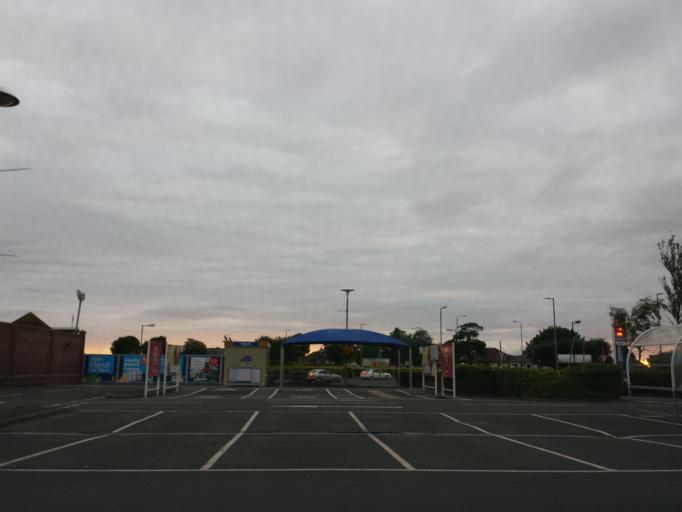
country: GB
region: Scotland
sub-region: South Ayrshire
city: Prestwick
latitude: 55.4683
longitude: -4.6084
